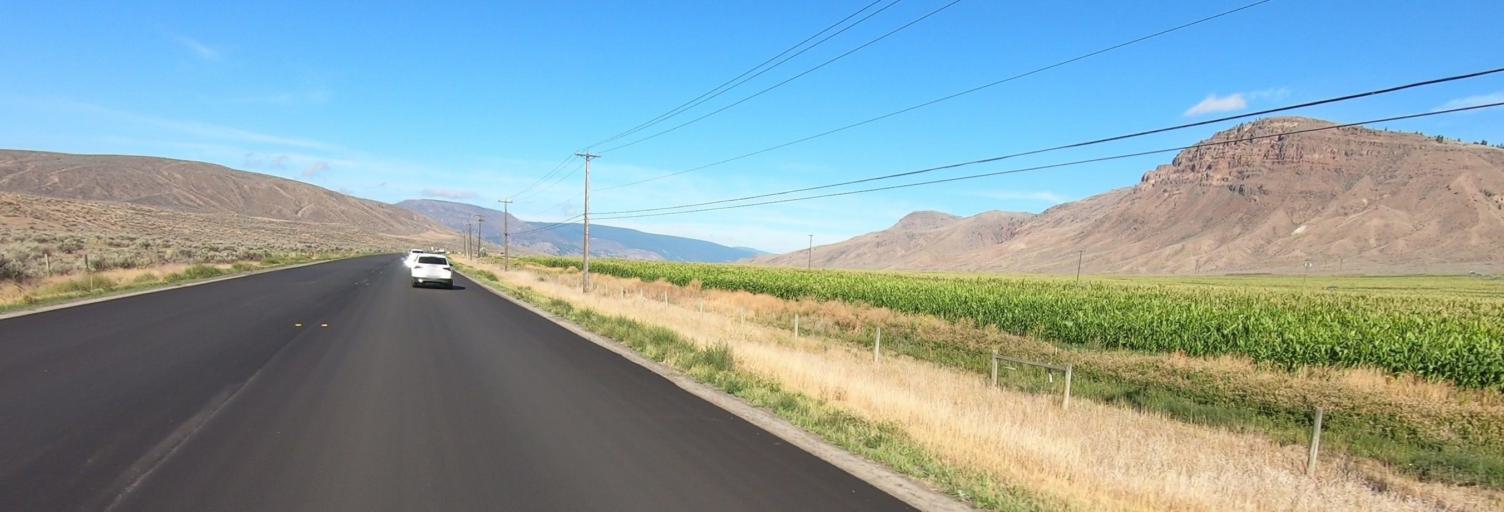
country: CA
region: British Columbia
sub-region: Thompson-Nicola Regional District
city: Ashcroft
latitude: 50.7862
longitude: -121.2095
